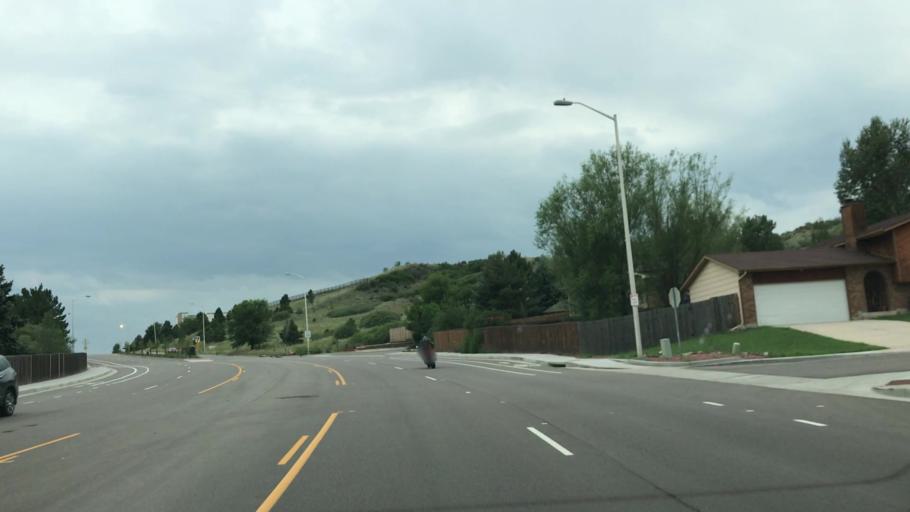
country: US
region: Colorado
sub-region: El Paso County
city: Colorado Springs
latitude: 38.8853
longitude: -104.8475
